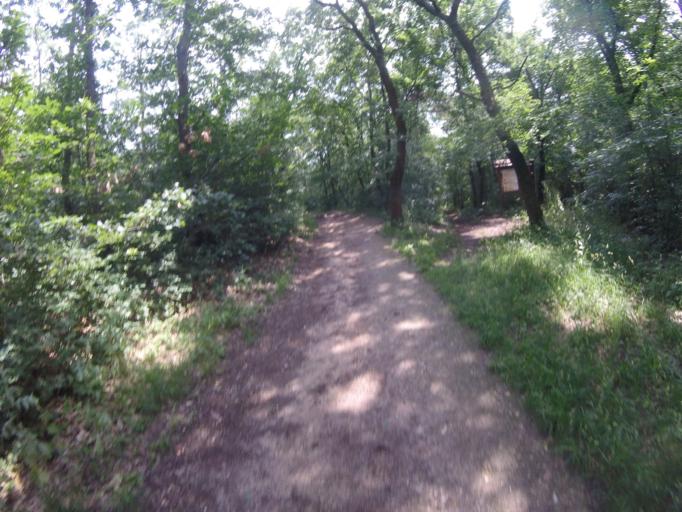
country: HU
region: Pest
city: Toeroekbalint
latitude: 47.4248
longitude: 18.9231
